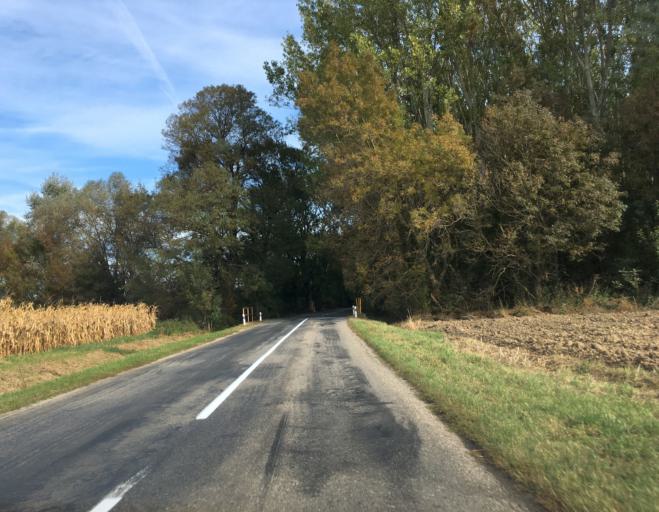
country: SK
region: Nitriansky
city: Svodin
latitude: 48.0043
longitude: 18.4133
